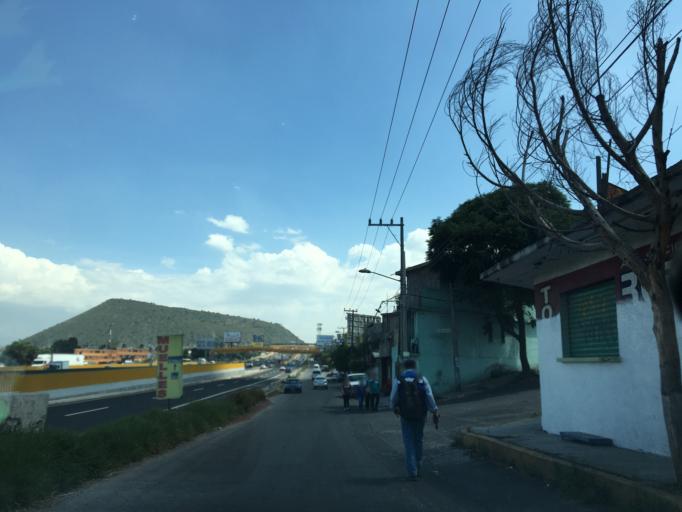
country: MX
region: Mexico
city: Los Reyes La Paz
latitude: 19.3536
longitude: -98.9899
